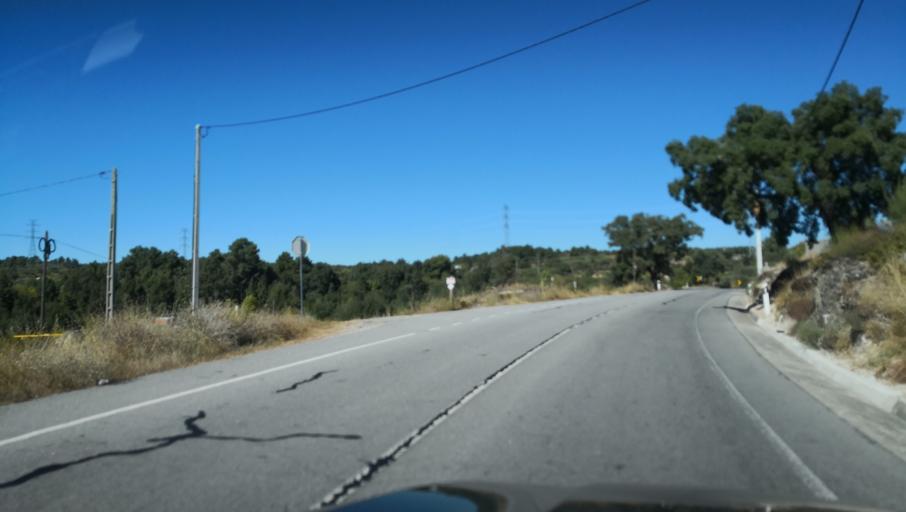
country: PT
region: Vila Real
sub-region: Valpacos
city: Valpacos
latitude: 41.6372
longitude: -7.3173
